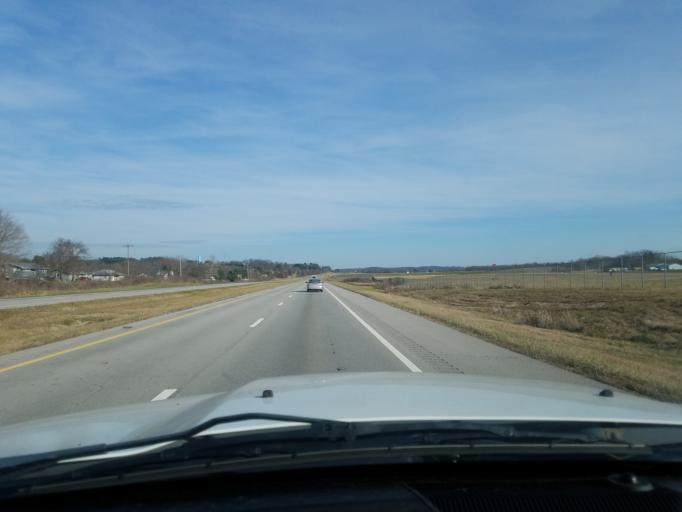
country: US
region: Ohio
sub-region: Athens County
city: Athens
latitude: 39.2153
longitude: -82.2249
